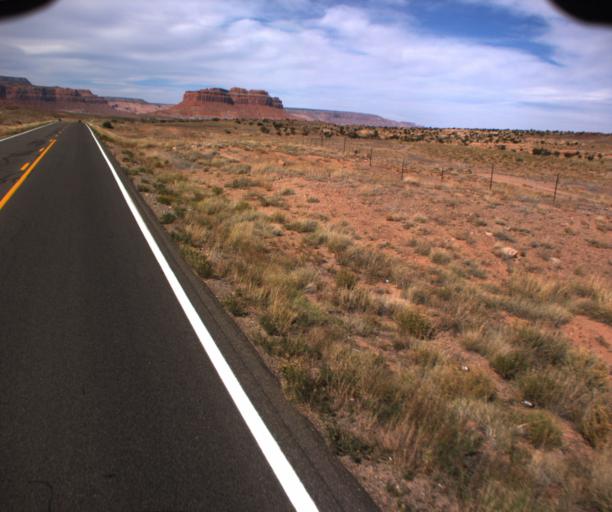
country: US
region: Arizona
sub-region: Navajo County
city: Kayenta
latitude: 36.8354
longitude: -110.2511
